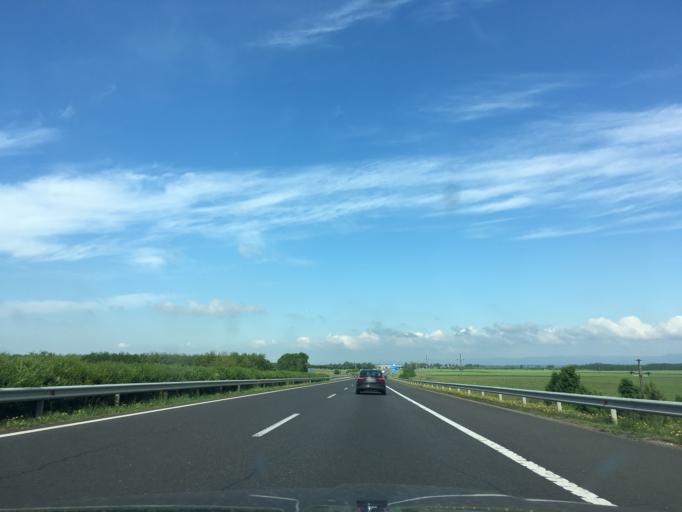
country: HU
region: Borsod-Abauj-Zemplen
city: Hejobaba
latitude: 47.8764
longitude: 20.9188
